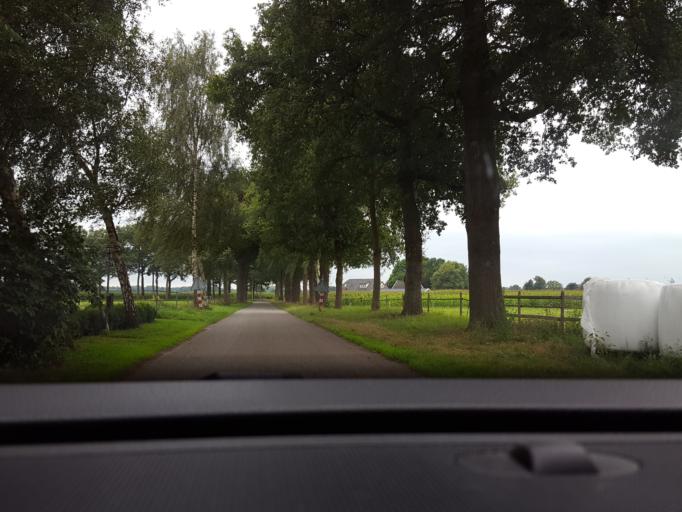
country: NL
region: Gelderland
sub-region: Gemeente Zutphen
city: Leesten
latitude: 52.1160
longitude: 6.2420
